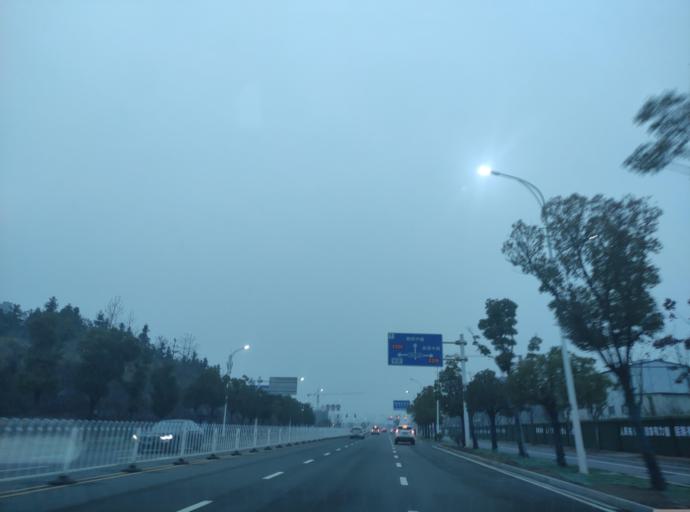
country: CN
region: Jiangxi Sheng
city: Pingxiang
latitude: 27.6704
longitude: 113.8550
